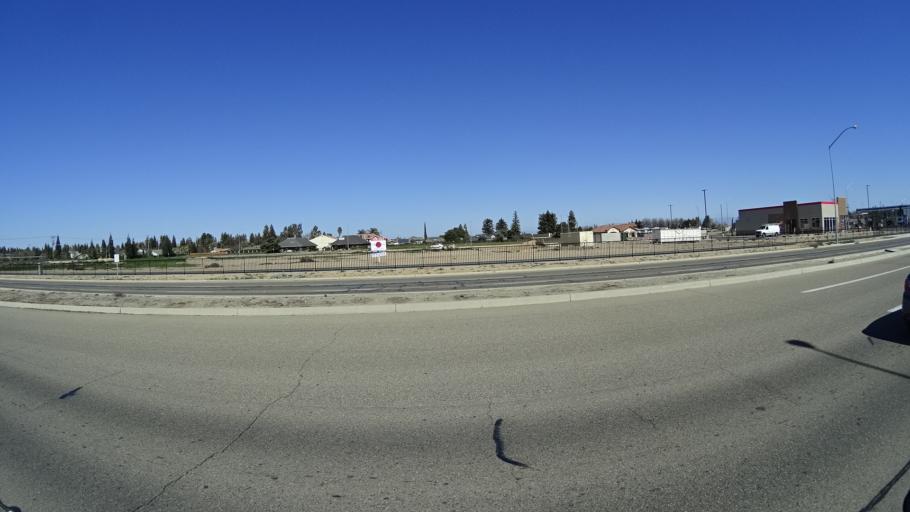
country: US
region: California
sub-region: Fresno County
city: West Park
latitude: 36.8370
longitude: -119.8727
